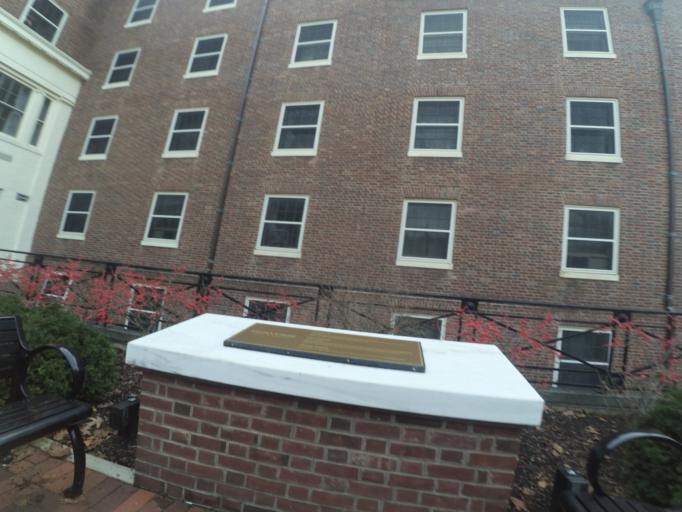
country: US
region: Pennsylvania
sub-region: Centre County
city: State College
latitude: 40.7979
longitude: -77.8586
